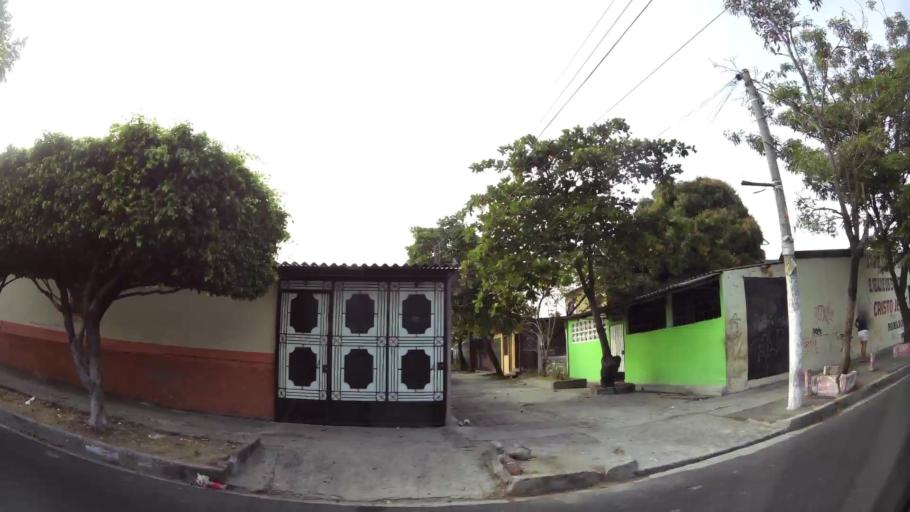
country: SV
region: San Salvador
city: Soyapango
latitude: 13.7247
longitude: -89.1271
